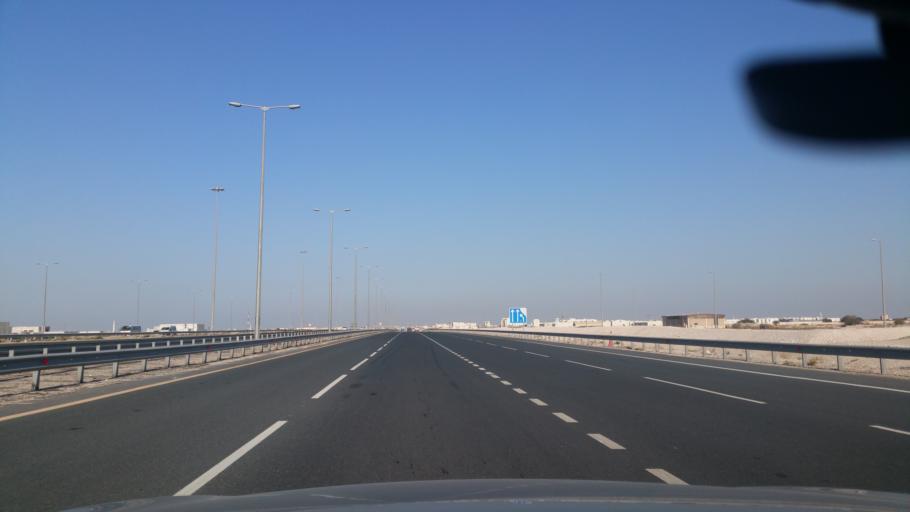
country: QA
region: Baladiyat ar Rayyan
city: Ar Rayyan
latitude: 25.1757
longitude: 51.3381
